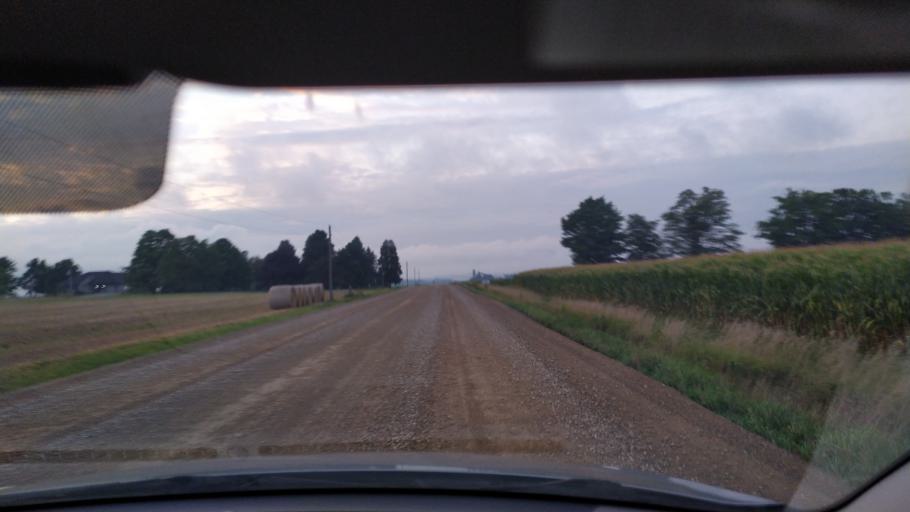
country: CA
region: Ontario
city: Kitchener
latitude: 43.3159
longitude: -80.6136
